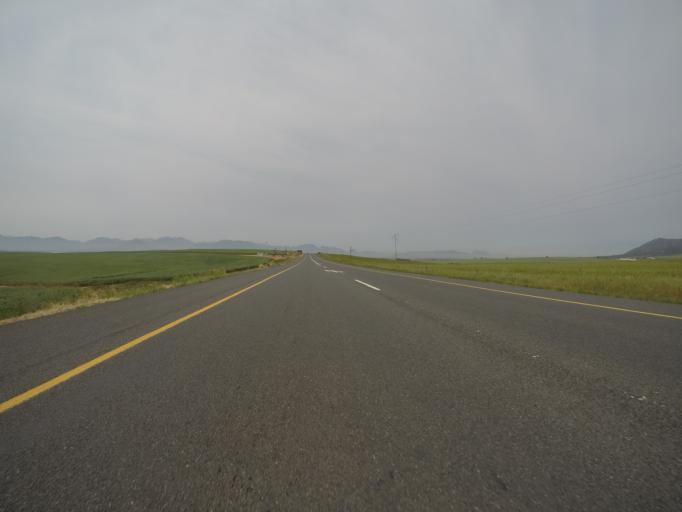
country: ZA
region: Western Cape
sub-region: West Coast District Municipality
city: Malmesbury
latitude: -33.5478
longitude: 18.8660
